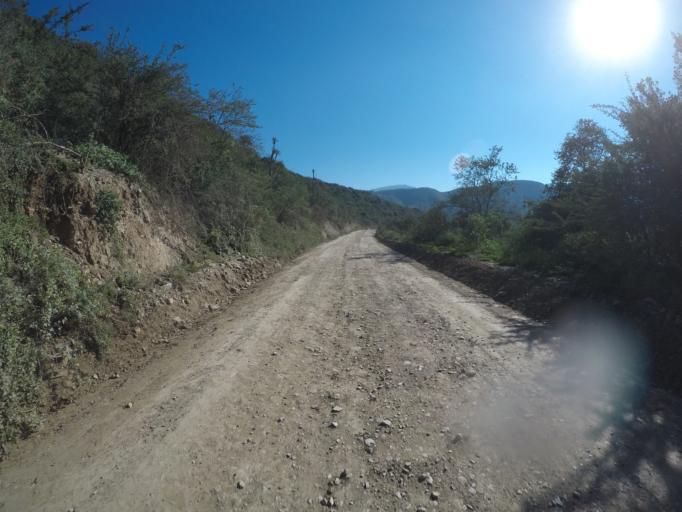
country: ZA
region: Eastern Cape
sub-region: Cacadu District Municipality
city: Kruisfontein
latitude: -33.6678
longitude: 24.5680
